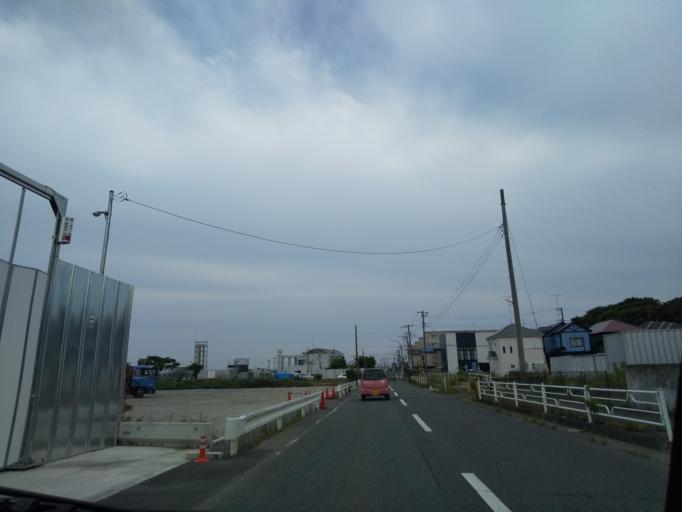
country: JP
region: Kanagawa
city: Atsugi
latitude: 35.4753
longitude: 139.3531
